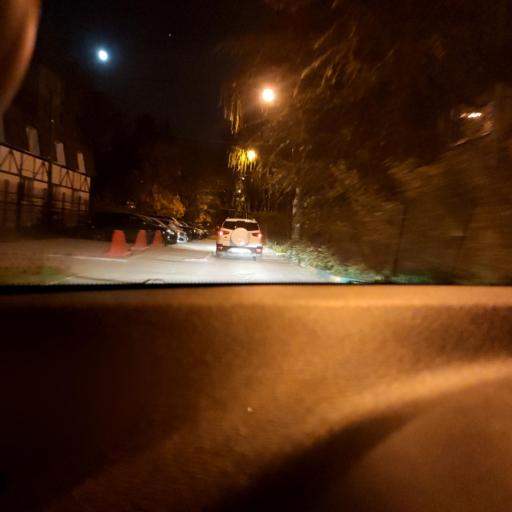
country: RU
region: Samara
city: Samara
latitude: 53.1922
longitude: 50.1272
